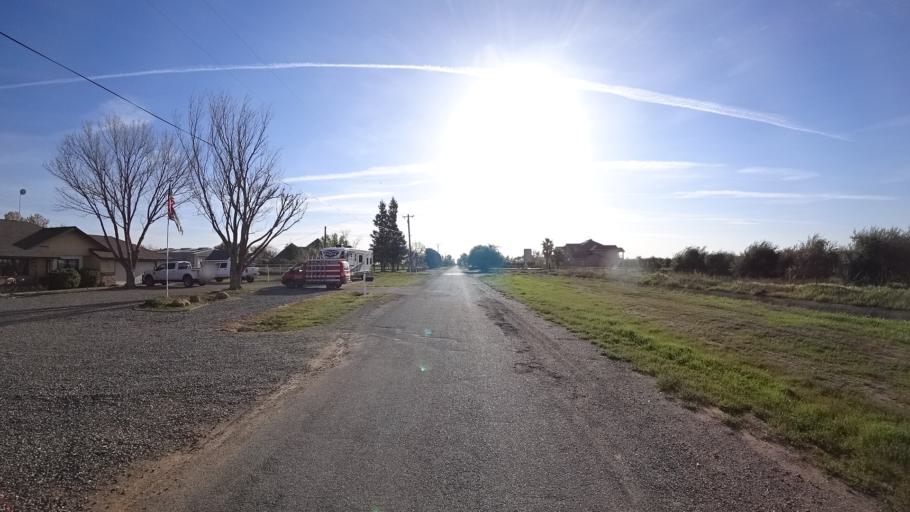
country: US
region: California
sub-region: Glenn County
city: Orland
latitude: 39.7333
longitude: -122.2200
